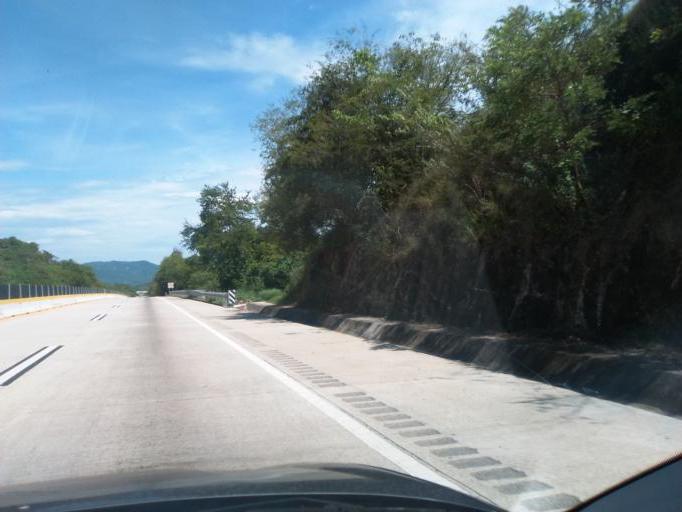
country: MX
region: Guerrero
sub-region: Acapulco de Juarez
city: Kilometro 30
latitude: 16.9693
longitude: -99.7294
